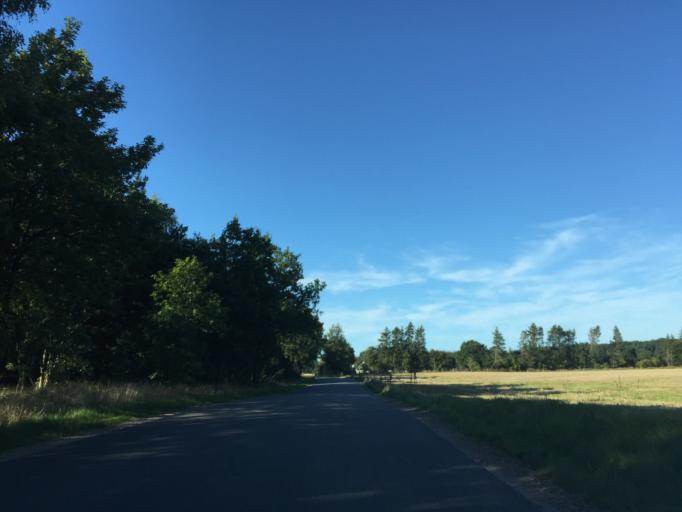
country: DK
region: Central Jutland
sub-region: Silkeborg Kommune
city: Svejbaek
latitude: 56.2193
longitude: 9.6824
